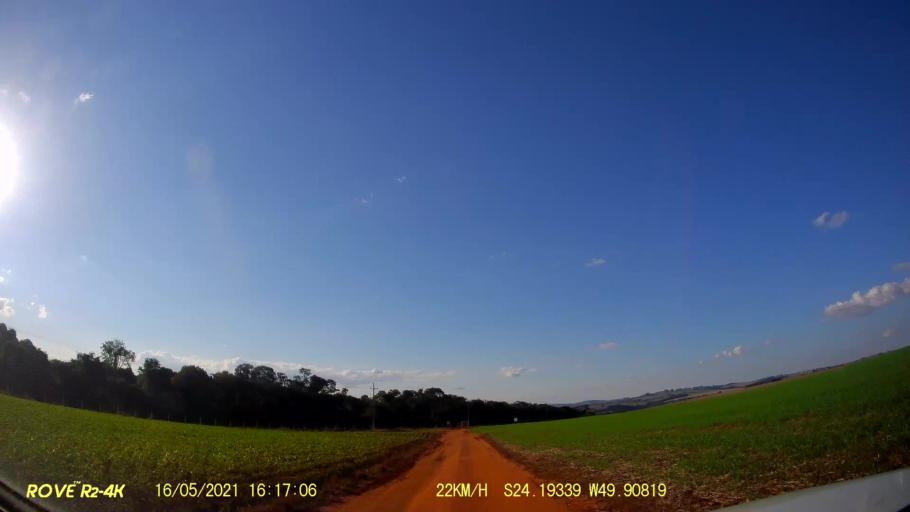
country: BR
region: Parana
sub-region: Jaguariaiva
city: Jaguariaiva
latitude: -24.1931
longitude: -49.9084
